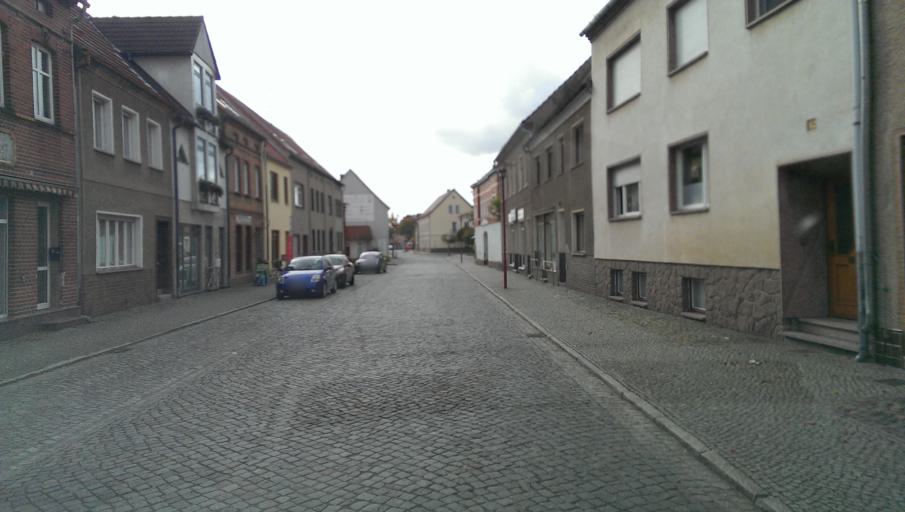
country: DE
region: Brandenburg
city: Doberlug-Kirchhain
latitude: 51.6348
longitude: 13.5606
